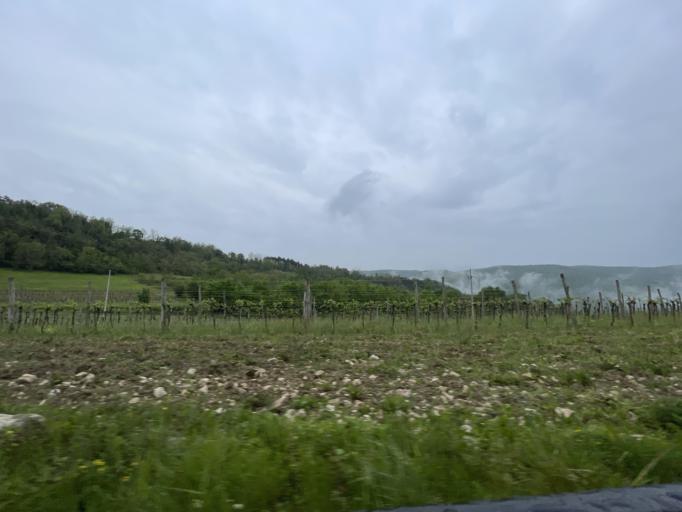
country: HR
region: Istarska
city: Karojba
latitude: 45.3283
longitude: 13.8072
